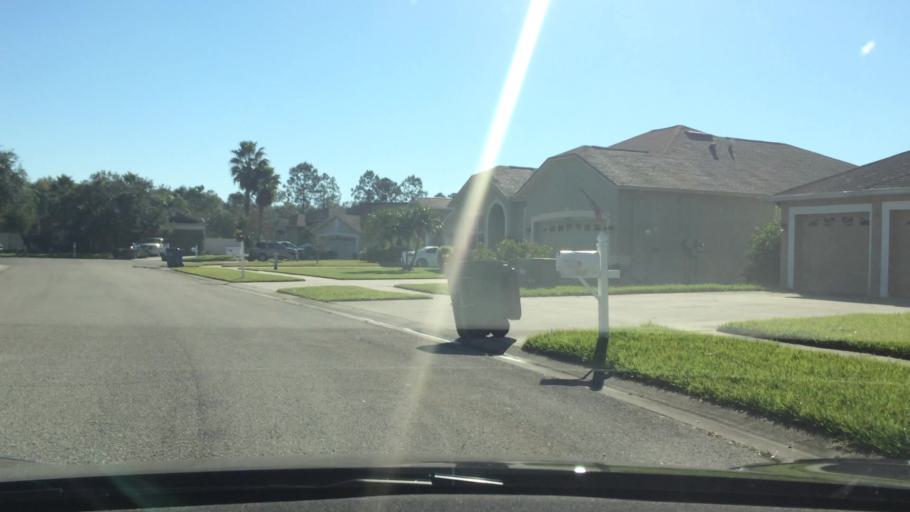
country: US
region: Florida
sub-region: Pasco County
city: Land O' Lakes
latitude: 28.2086
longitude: -82.3960
